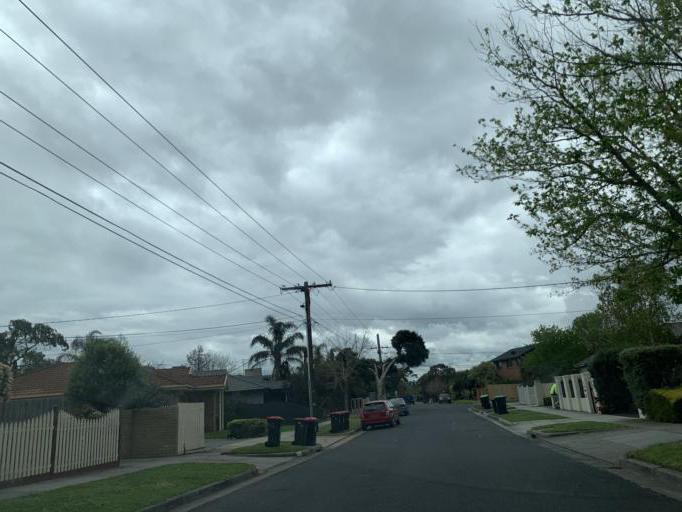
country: AU
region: Victoria
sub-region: Kingston
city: Mentone
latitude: -37.9734
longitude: 145.0766
